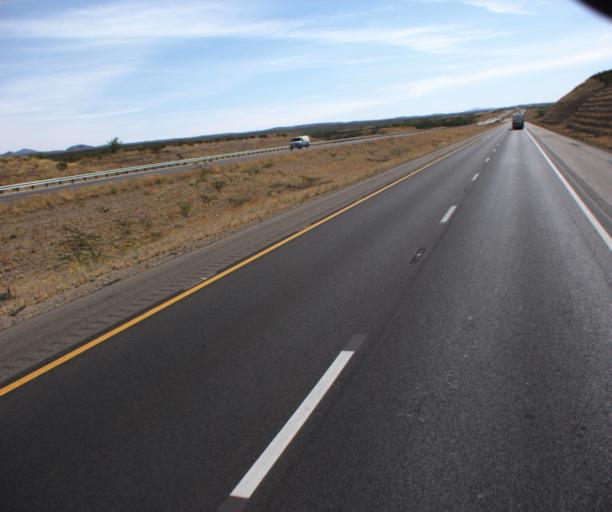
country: US
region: Arizona
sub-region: Cochise County
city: Mescal
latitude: 31.9865
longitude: -110.5753
